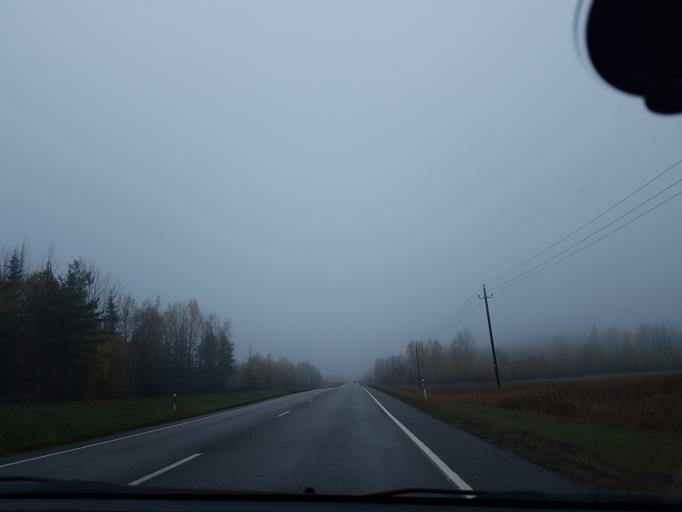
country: FI
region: Uusimaa
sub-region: Helsinki
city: Jaervenpaeae
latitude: 60.4551
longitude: 25.1370
